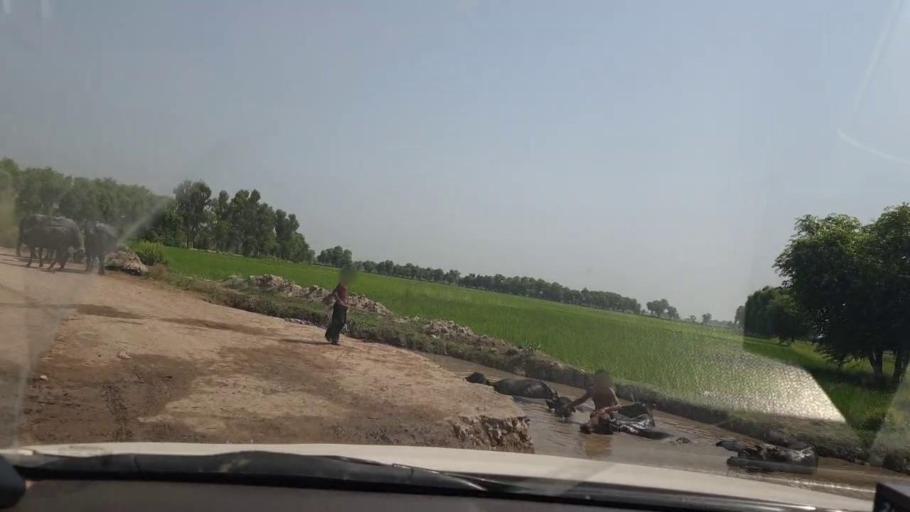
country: PK
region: Sindh
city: Chak
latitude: 27.8826
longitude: 68.7831
